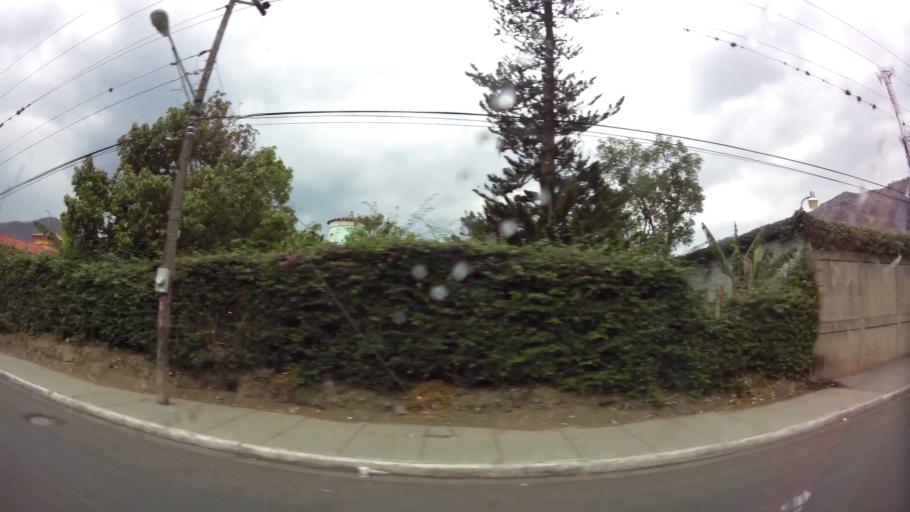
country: NI
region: Jinotega
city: Jinotega
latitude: 13.0914
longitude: -85.9986
